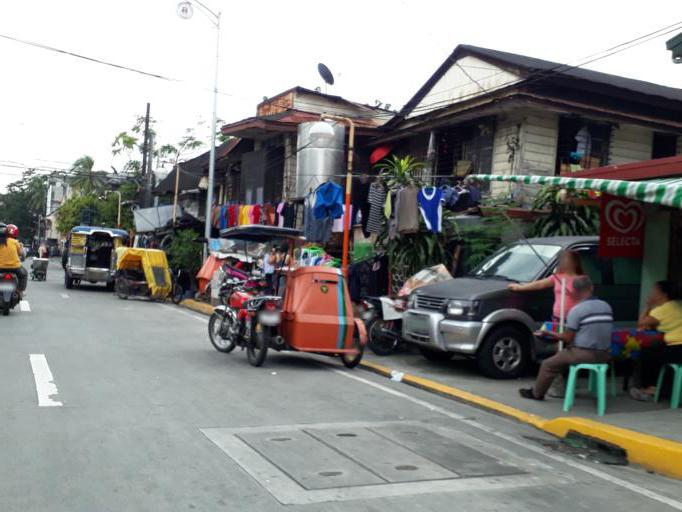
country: PH
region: Metro Manila
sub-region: City of Manila
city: Manila
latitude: 14.6077
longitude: 120.9989
